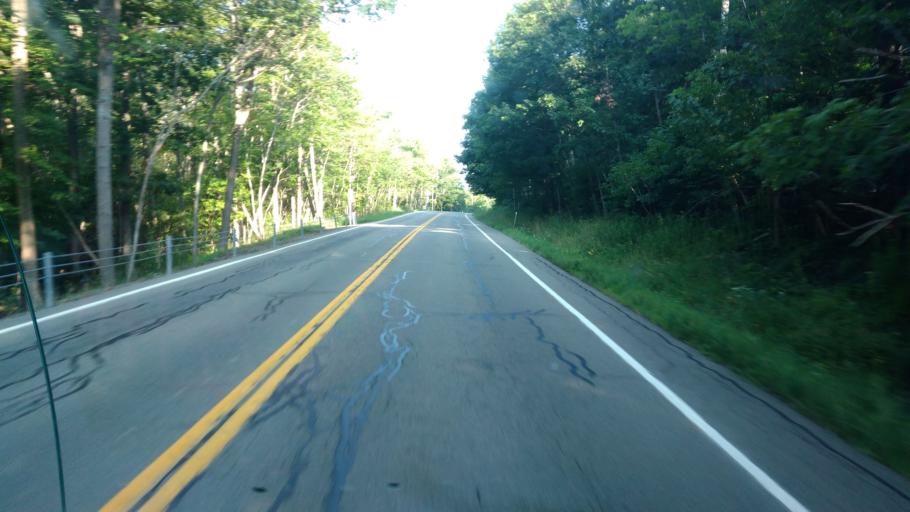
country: US
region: New York
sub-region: Allegany County
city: Andover
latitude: 42.1487
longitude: -77.6890
